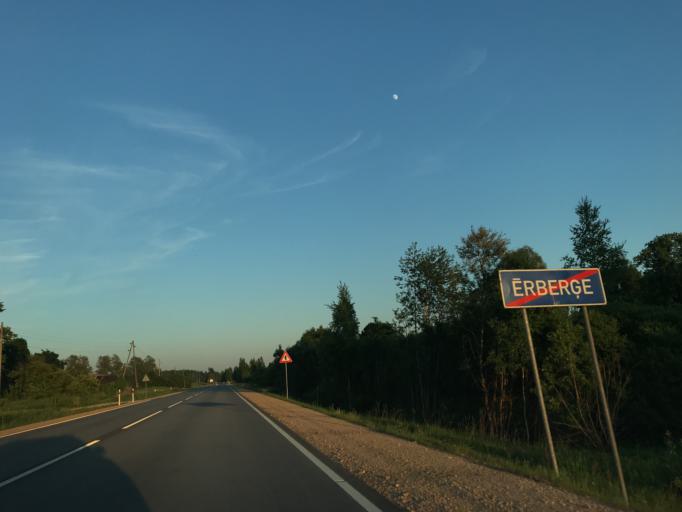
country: LV
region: Jaunjelgava
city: Jaunjelgava
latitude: 56.3663
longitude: 25.0318
